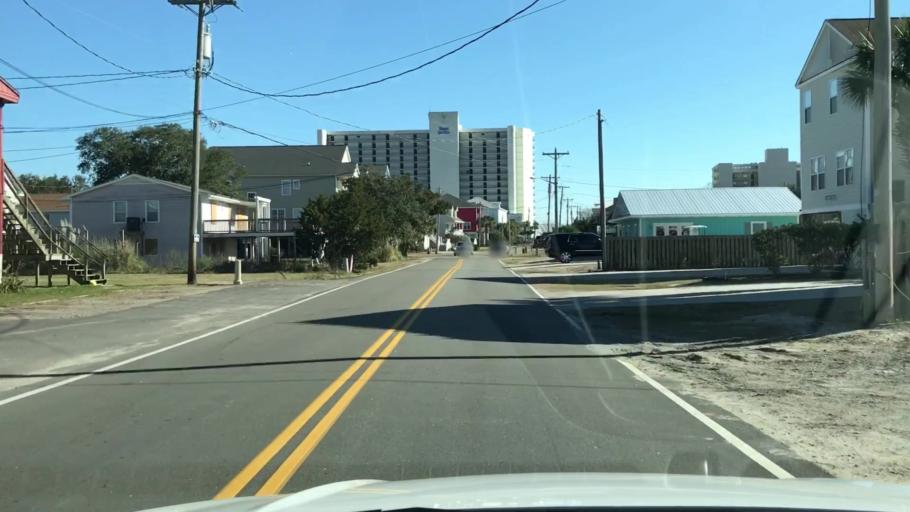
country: US
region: South Carolina
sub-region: Horry County
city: Garden City
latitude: 33.5872
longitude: -78.9931
